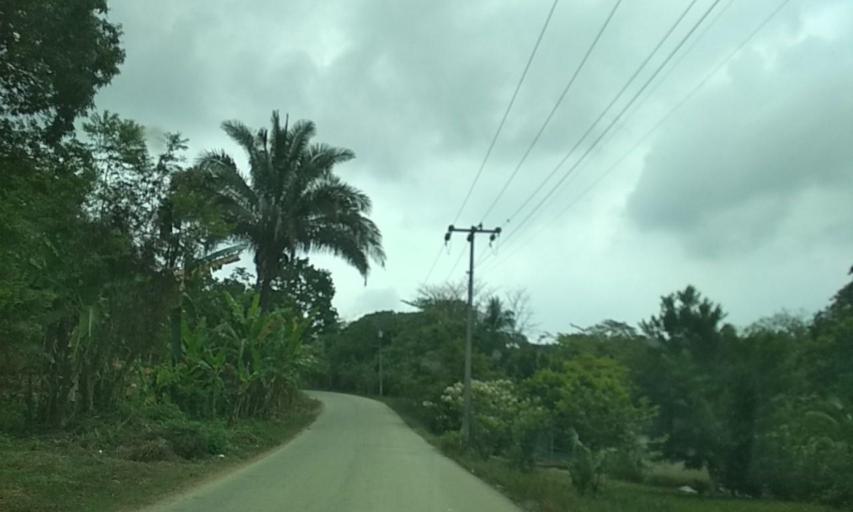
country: MX
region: Veracruz
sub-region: Uxpanapa
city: Poblado 10
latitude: 17.4753
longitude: -94.1201
